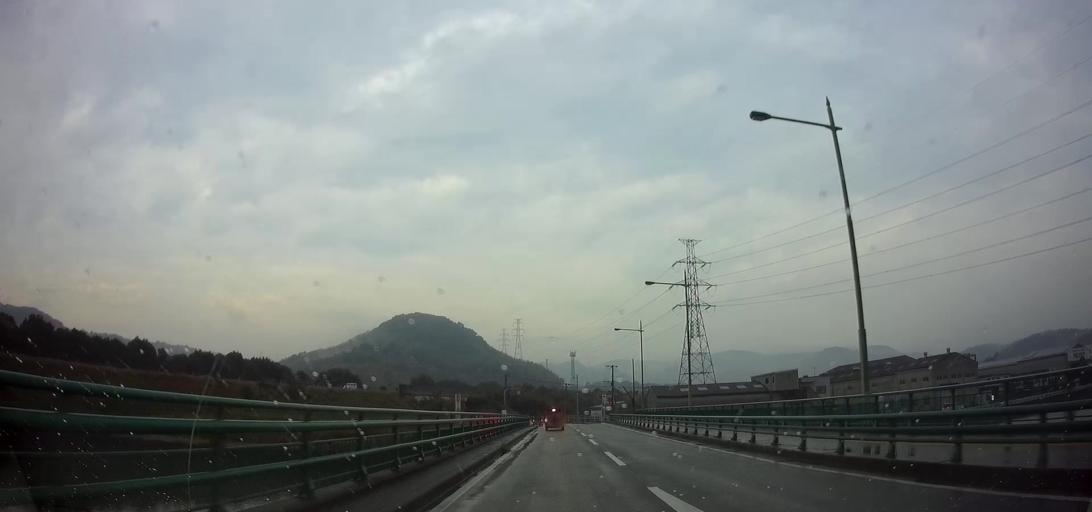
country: JP
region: Nagasaki
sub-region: Isahaya-shi
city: Isahaya
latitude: 32.8481
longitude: 130.0107
